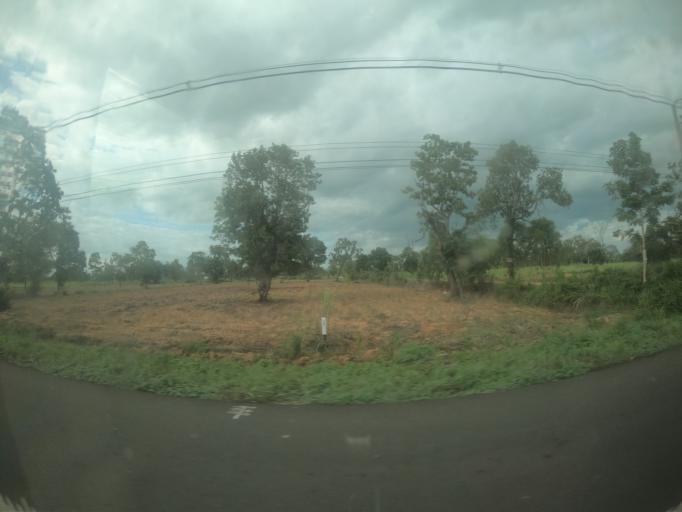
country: TH
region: Surin
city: Kap Choeng
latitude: 14.5423
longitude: 103.5185
